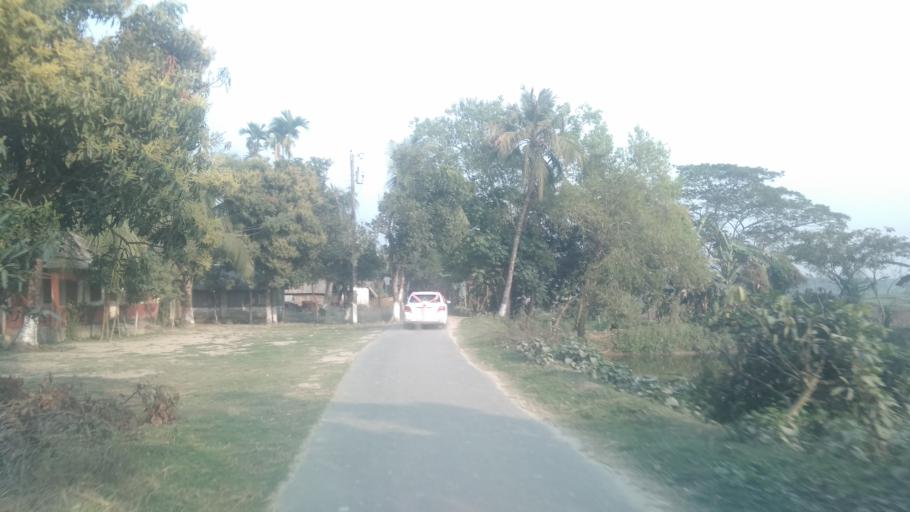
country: BD
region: Dhaka
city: Netrakona
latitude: 24.7752
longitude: 90.6072
